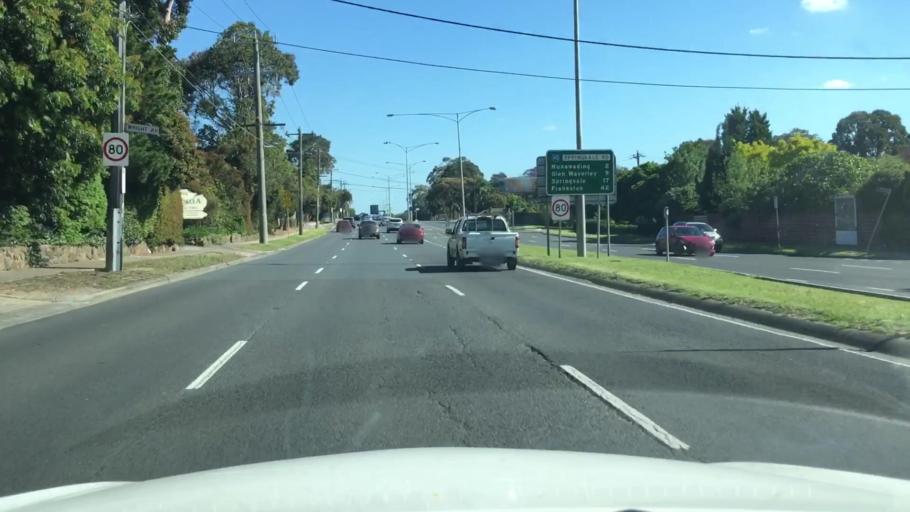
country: AU
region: Victoria
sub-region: Manningham
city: Donvale
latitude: -37.7973
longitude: 145.1789
